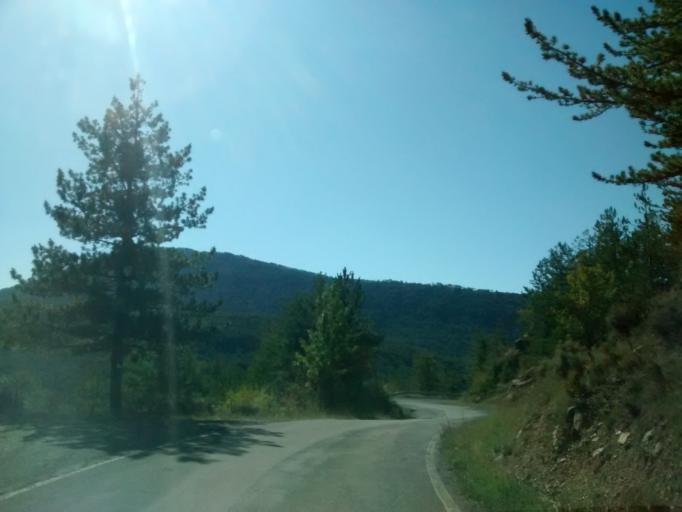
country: ES
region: Aragon
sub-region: Provincia de Huesca
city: Jaca
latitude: 42.4977
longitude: -0.5547
